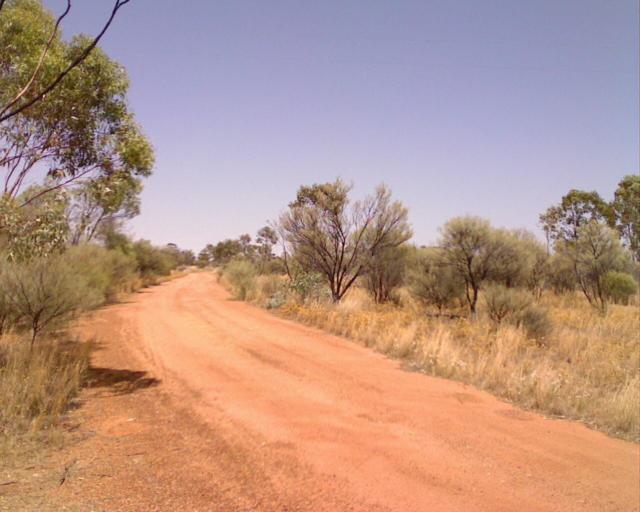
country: AU
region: Western Australia
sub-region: Merredin
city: Merredin
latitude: -30.9224
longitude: 118.2022
